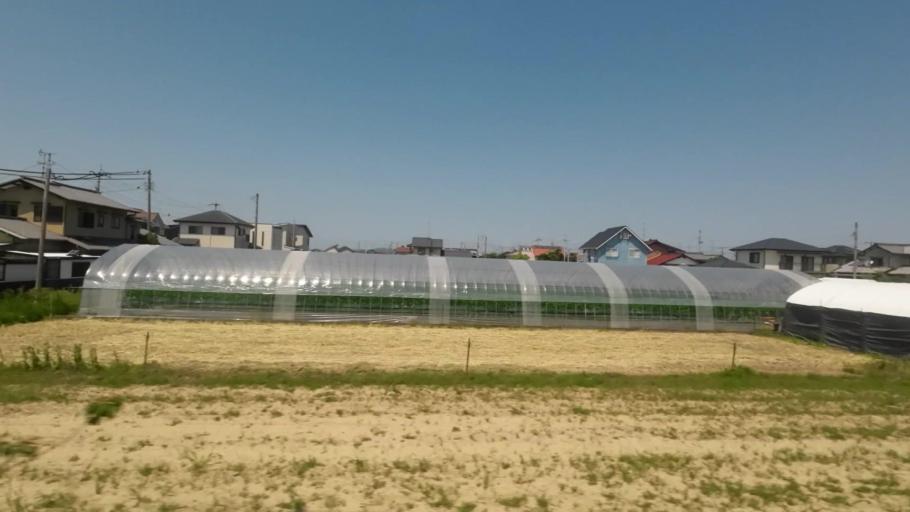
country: JP
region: Ehime
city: Hojo
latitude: 33.9352
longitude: 132.7670
